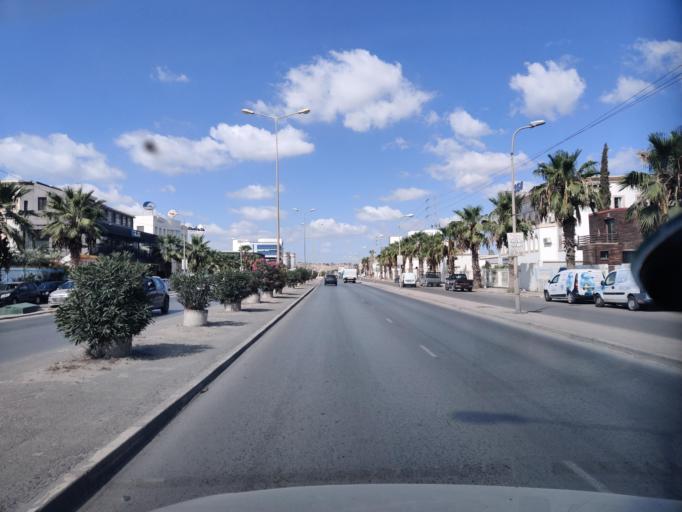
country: TN
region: Bin 'Arus
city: Ben Arous
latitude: 36.7747
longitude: 10.2173
